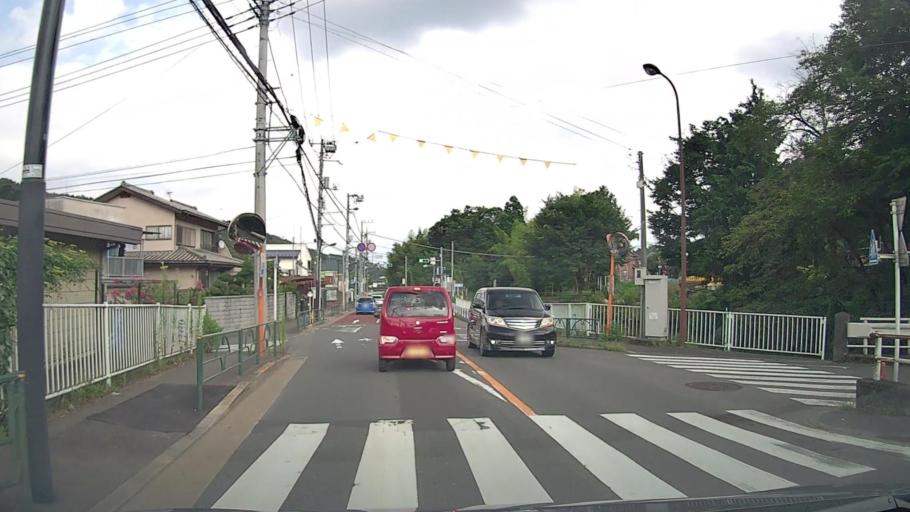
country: JP
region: Tokyo
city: Itsukaichi
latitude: 35.7024
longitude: 139.2583
